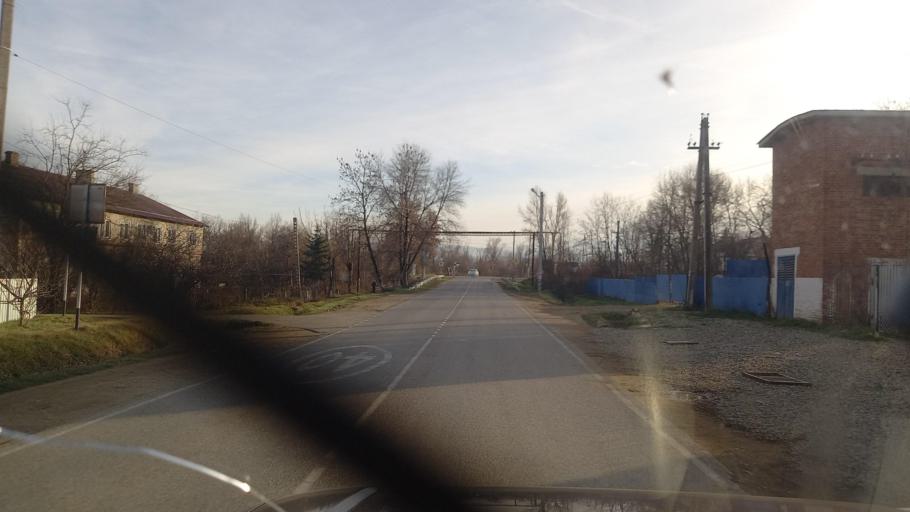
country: RU
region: Krasnodarskiy
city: Khadyzhensk
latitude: 44.4444
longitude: 39.5245
